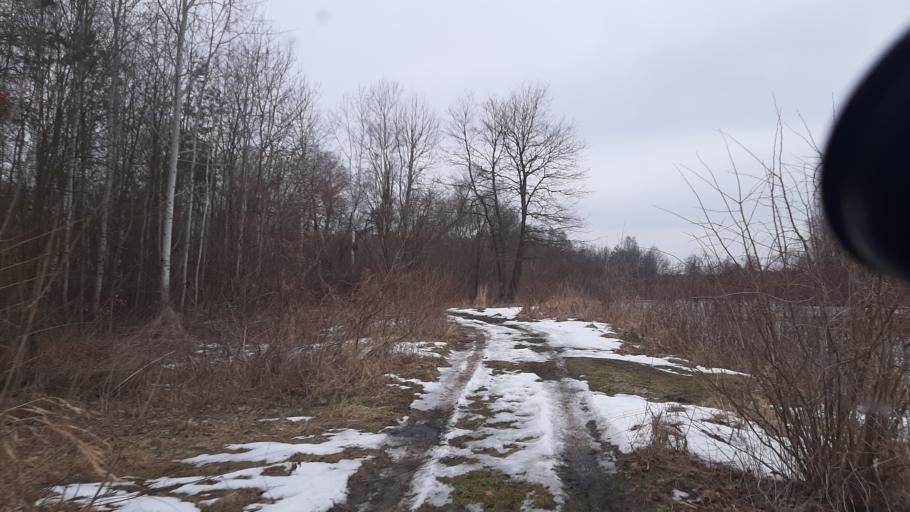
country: PL
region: Lublin Voivodeship
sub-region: Powiat wlodawski
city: Wlodawa
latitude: 51.5097
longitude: 23.6167
